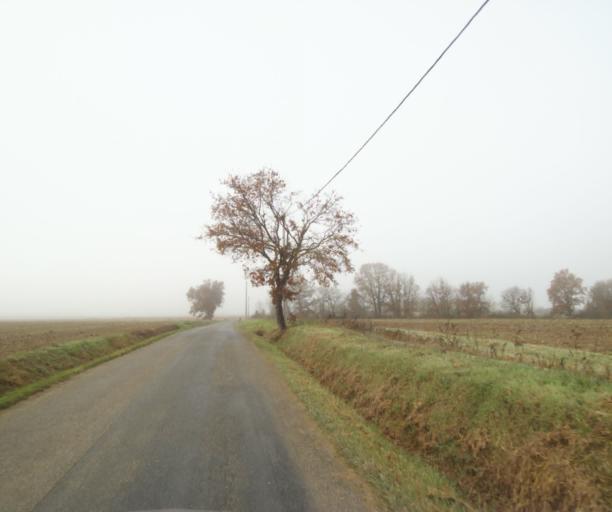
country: FR
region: Midi-Pyrenees
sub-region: Departement de la Haute-Garonne
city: Villaudric
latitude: 43.8301
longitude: 1.4720
